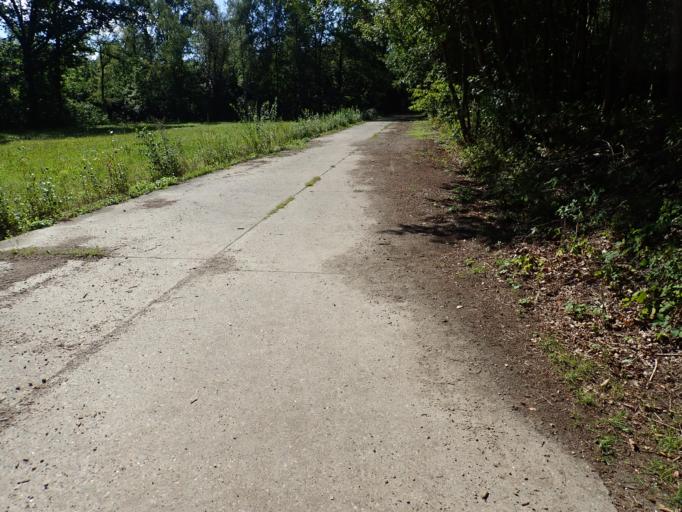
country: BE
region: Flanders
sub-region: Provincie Antwerpen
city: Westerlo
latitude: 51.1259
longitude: 4.8982
